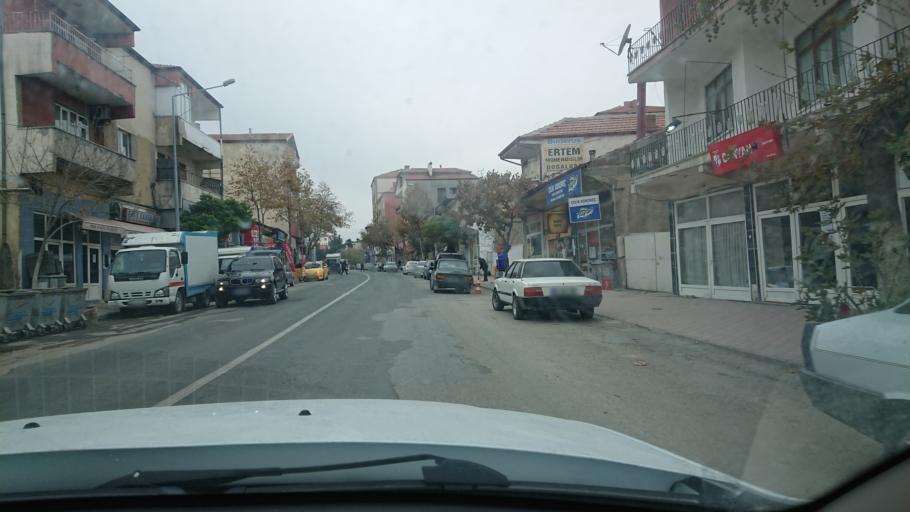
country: TR
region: Aksaray
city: Ortakoy
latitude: 38.7377
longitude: 34.0406
